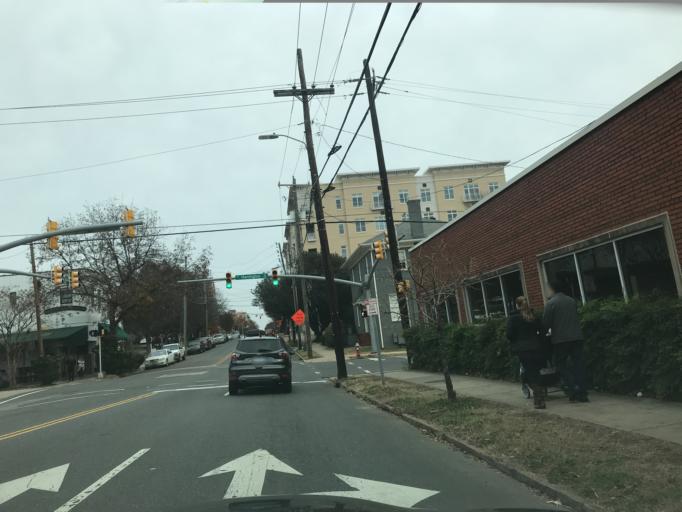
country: US
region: North Carolina
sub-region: Wake County
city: Raleigh
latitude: 35.7798
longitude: -78.6454
